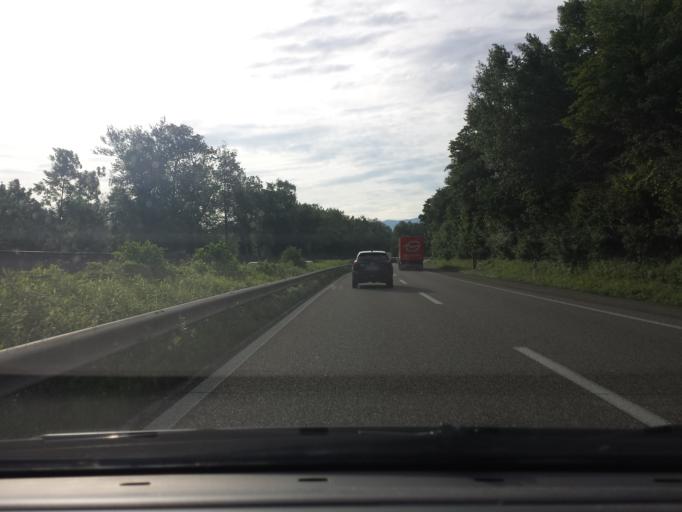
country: AT
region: Vorarlberg
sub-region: Politischer Bezirk Bregenz
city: Hochst
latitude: 47.4555
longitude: 9.6446
